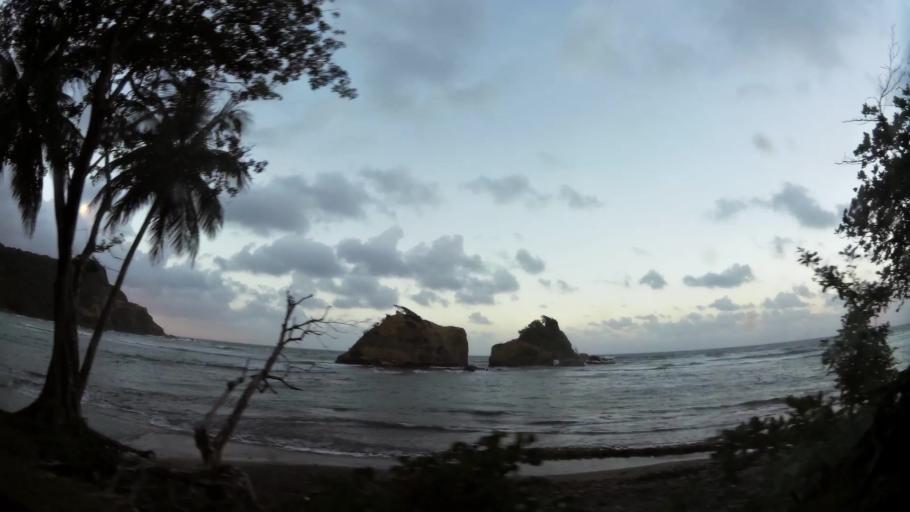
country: DM
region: Saint Andrew
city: Calibishie
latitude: 15.5930
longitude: -61.3540
